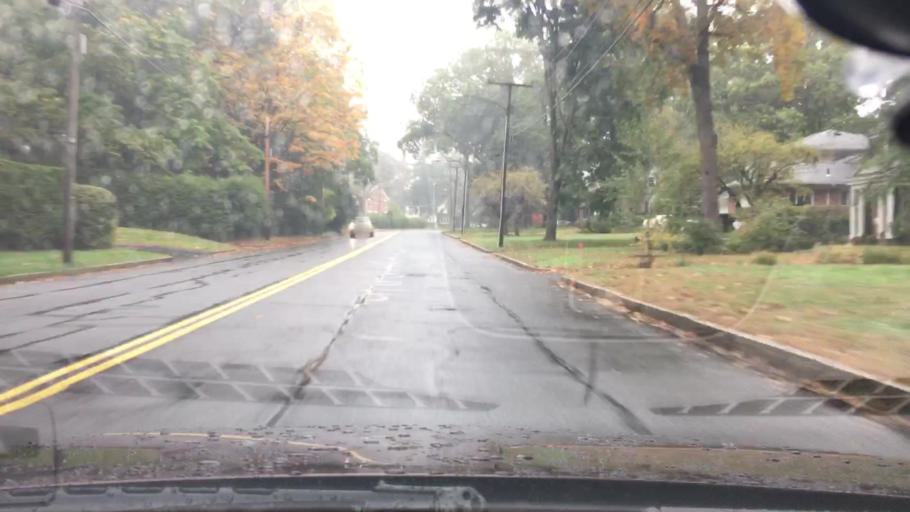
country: US
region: Massachusetts
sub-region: Hampden County
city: Longmeadow
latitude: 42.0751
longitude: -72.5524
